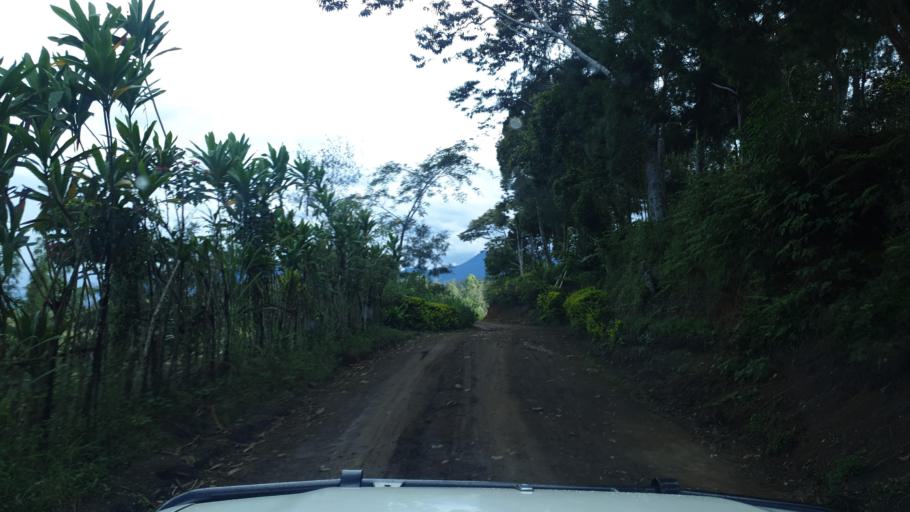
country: PG
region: Eastern Highlands
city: Goroka
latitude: -5.9227
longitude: 145.2641
